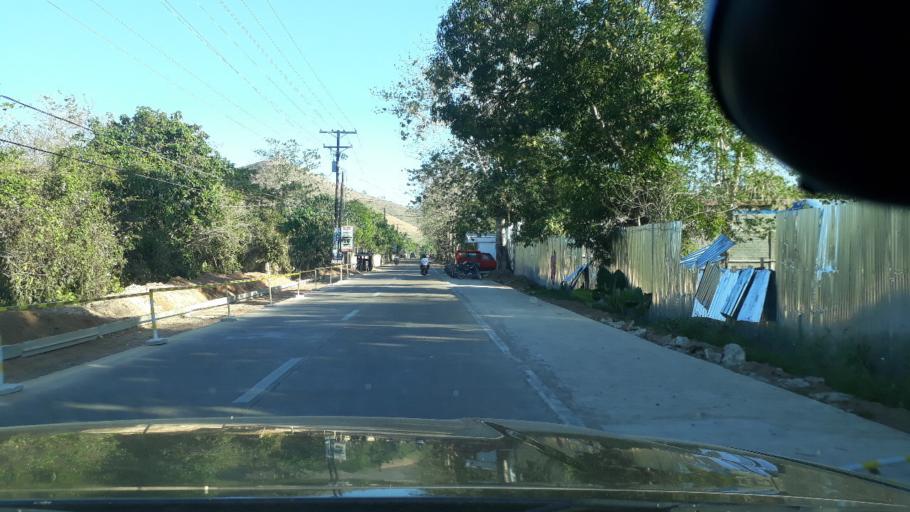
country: PH
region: Mimaropa
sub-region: Province of Palawan
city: Coron
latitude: 12.0111
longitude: 120.1966
